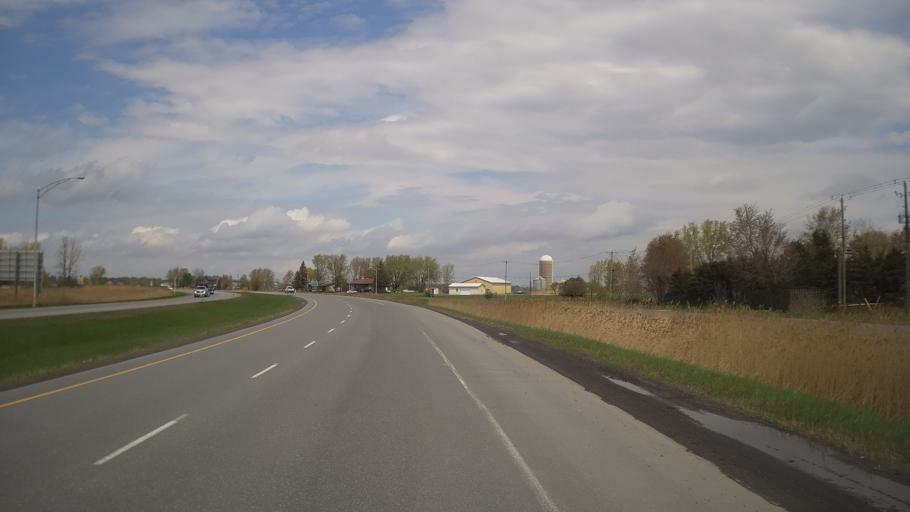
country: CA
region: Quebec
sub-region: Monteregie
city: Saint-Jean-sur-Richelieu
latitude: 45.3171
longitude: -73.2228
